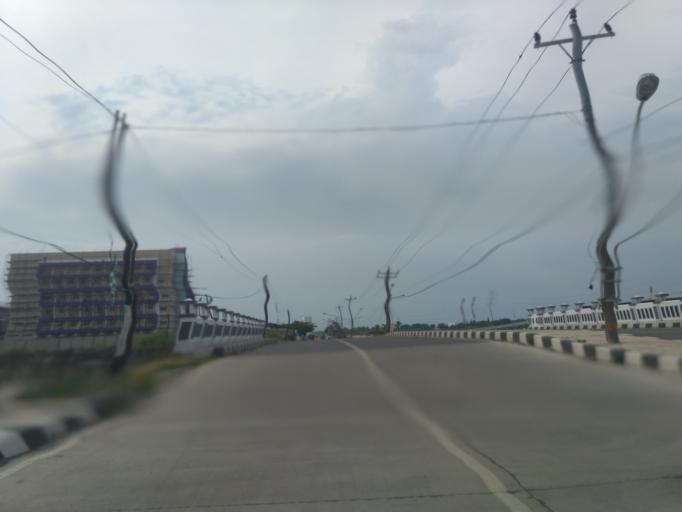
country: ID
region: Central Java
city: Semarang
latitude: -6.9650
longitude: 110.3994
